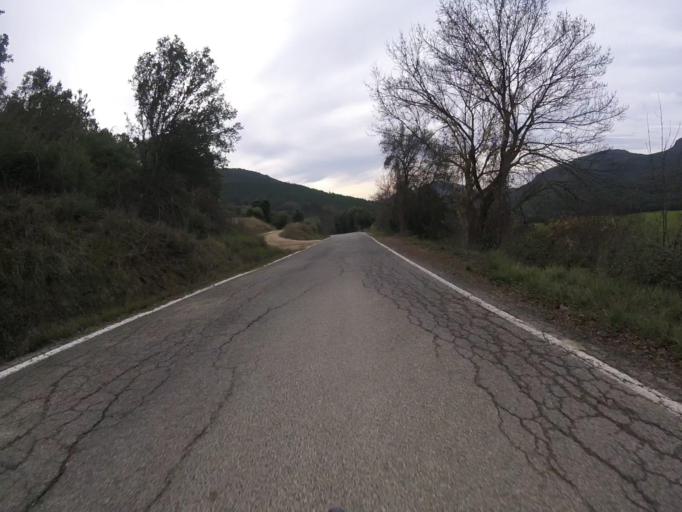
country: ES
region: Navarre
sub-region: Provincia de Navarra
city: Estella
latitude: 42.7131
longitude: -2.0454
